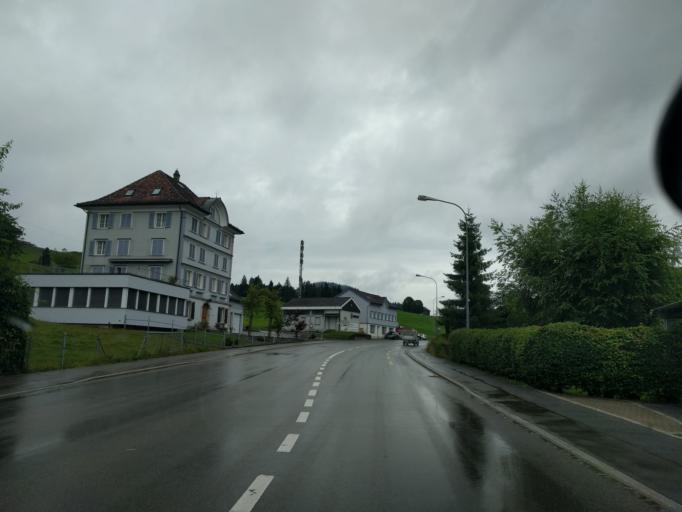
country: CH
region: Appenzell Ausserrhoden
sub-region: Bezirk Hinterland
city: Schwellbrunn
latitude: 47.3292
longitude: 9.2270
